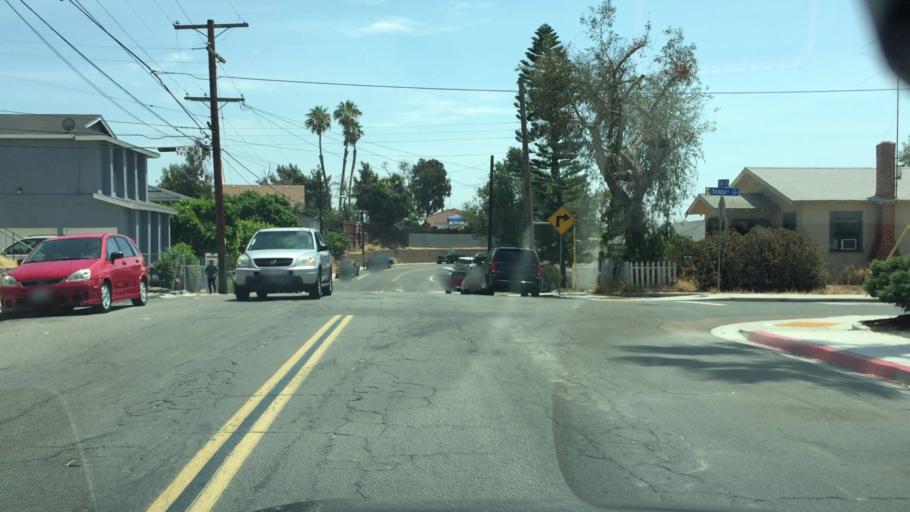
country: US
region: California
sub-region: San Diego County
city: Lemon Grove
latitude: 32.7466
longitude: -117.0832
